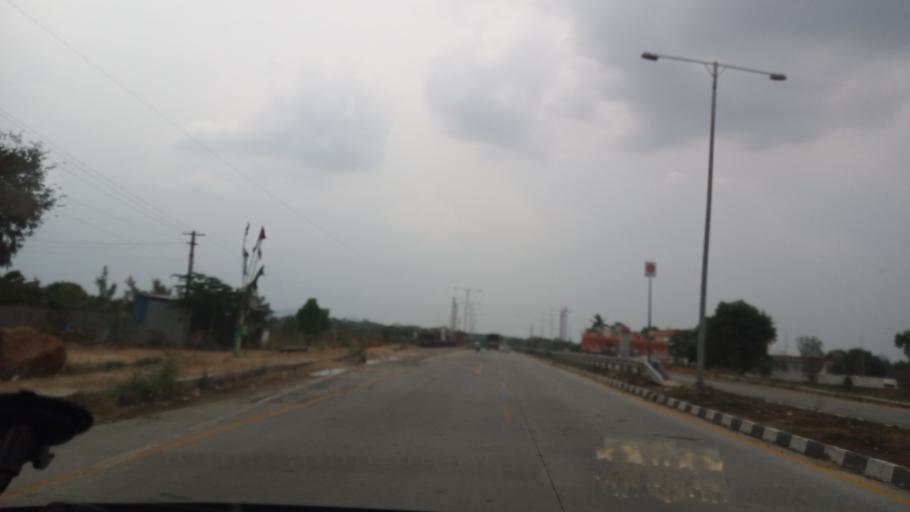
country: IN
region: Andhra Pradesh
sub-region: Chittoor
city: Palmaner
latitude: 13.1993
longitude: 78.7161
